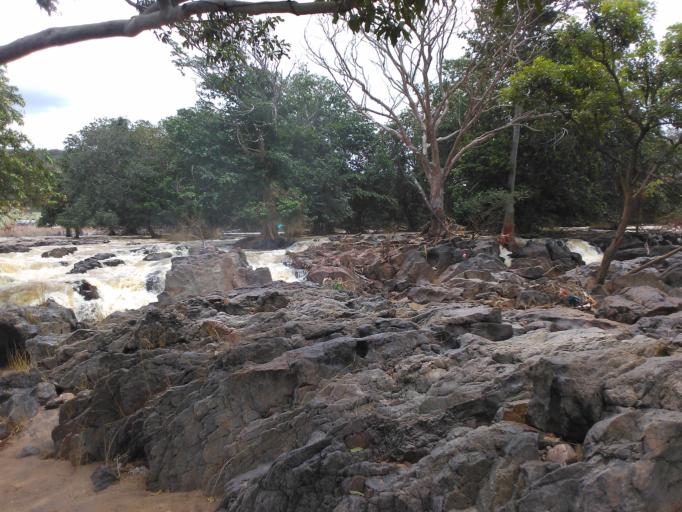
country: IN
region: Tamil Nadu
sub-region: Dharmapuri
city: Pennagaram
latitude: 12.1175
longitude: 77.7765
